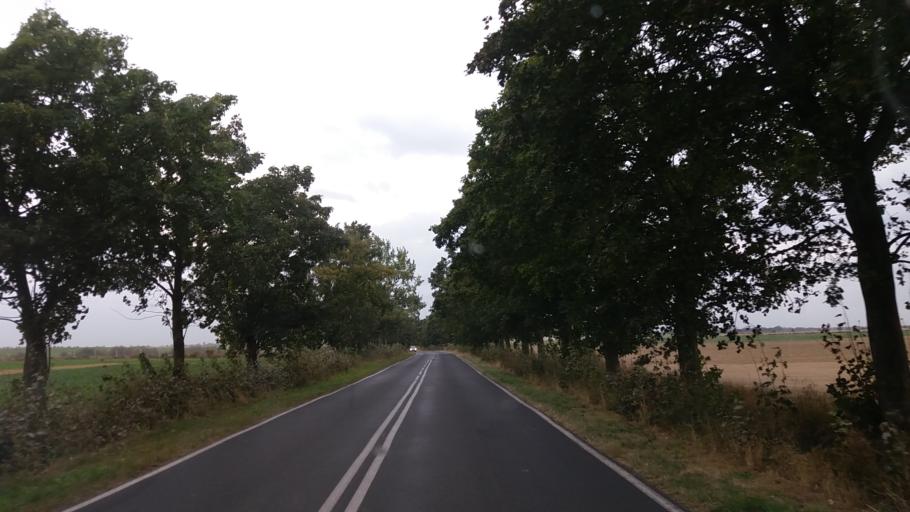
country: PL
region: Lubusz
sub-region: Powiat strzelecko-drezdenecki
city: Strzelce Krajenskie
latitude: 52.9117
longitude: 15.5589
